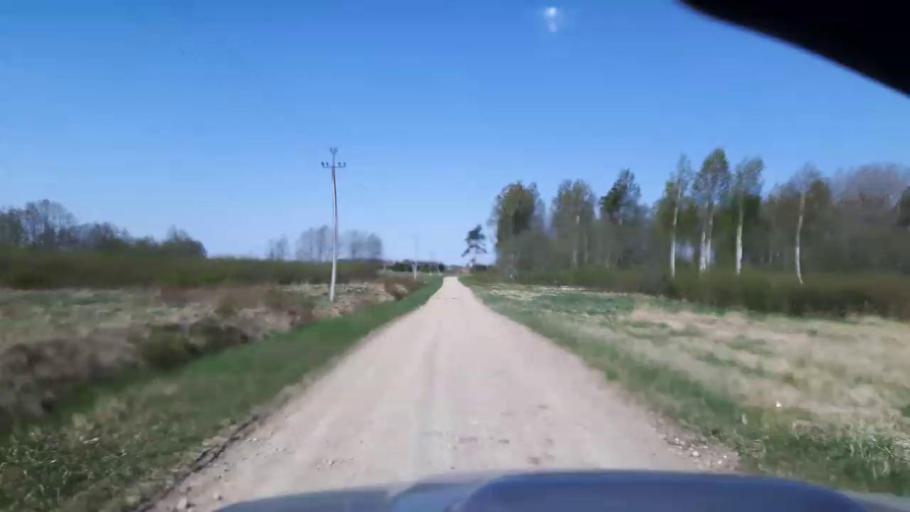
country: EE
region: Paernumaa
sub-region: Sindi linn
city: Sindi
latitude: 58.4443
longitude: 24.7890
